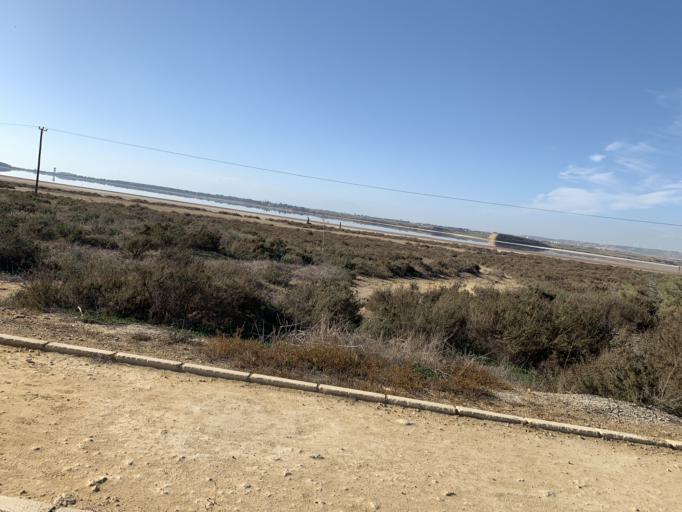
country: CY
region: Larnaka
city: Larnaca
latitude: 34.9039
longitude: 33.6243
